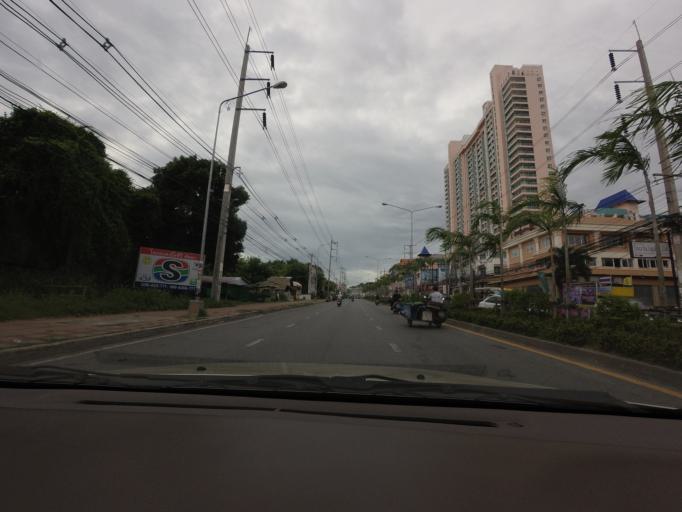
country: TH
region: Chon Buri
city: Phatthaya
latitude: 12.9064
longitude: 100.8690
